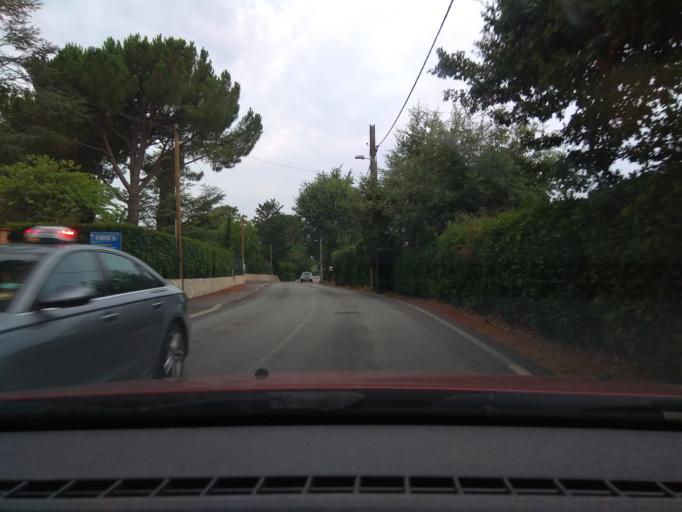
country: FR
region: Provence-Alpes-Cote d'Azur
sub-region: Departement des Alpes-Maritimes
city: Le Rouret
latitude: 43.6654
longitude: 7.0477
